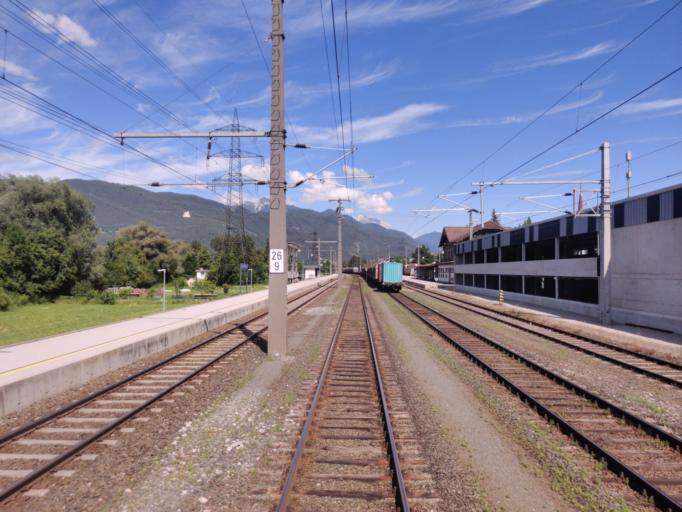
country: AT
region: Tyrol
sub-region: Politischer Bezirk Innsbruck Land
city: Pfaffenhofen
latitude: 47.3007
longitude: 11.0772
